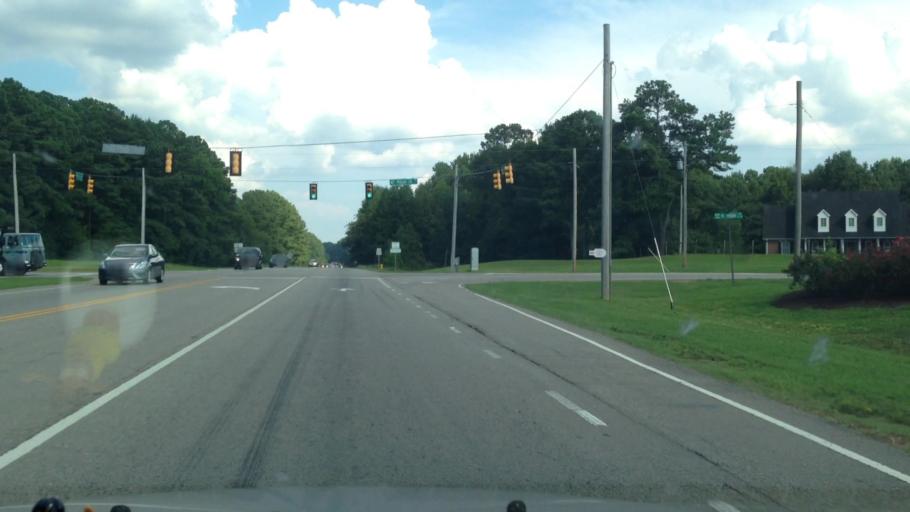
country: US
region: North Carolina
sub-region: Lee County
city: Broadway
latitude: 35.4445
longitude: -79.1106
